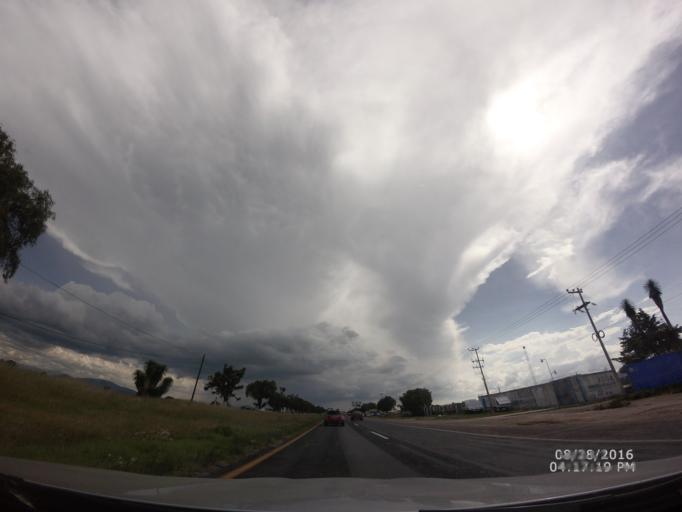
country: MX
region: Hidalgo
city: Zapotlan de Juarez
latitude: 19.9775
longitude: -98.8500
